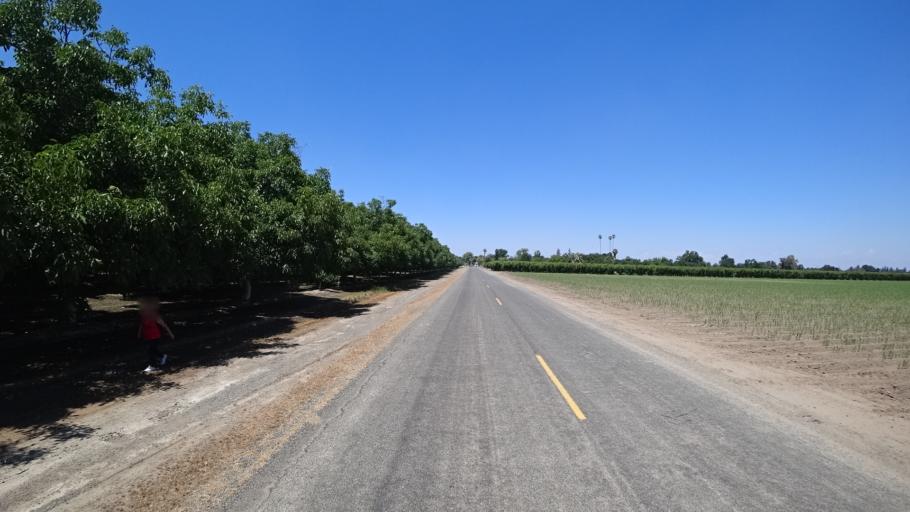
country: US
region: California
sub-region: Fresno County
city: Laton
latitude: 36.4199
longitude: -119.6952
